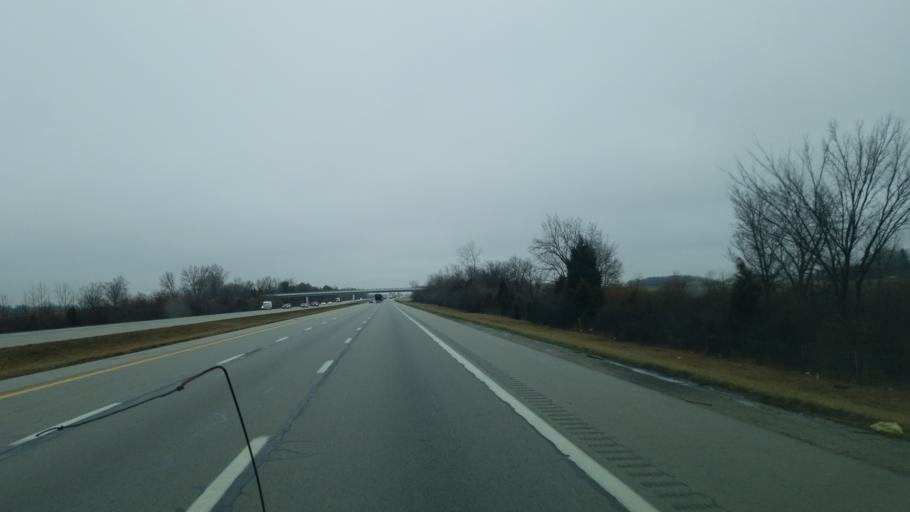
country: US
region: Ohio
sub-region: Fayette County
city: Jeffersonville
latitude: 39.6073
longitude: -83.6303
